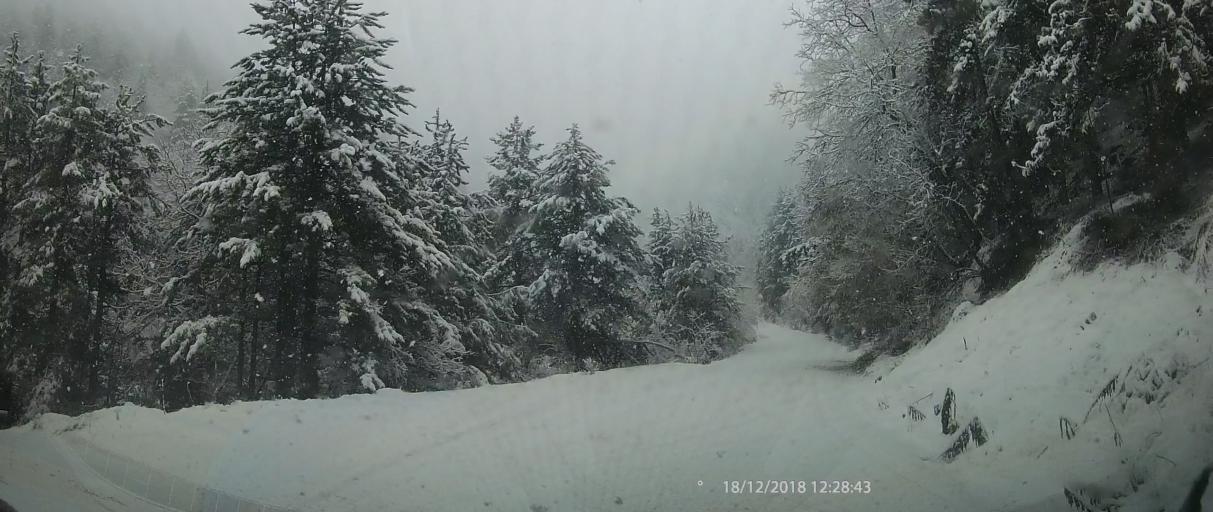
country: GR
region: Central Macedonia
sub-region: Nomos Pierias
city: Litochoro
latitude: 40.0858
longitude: 22.4069
